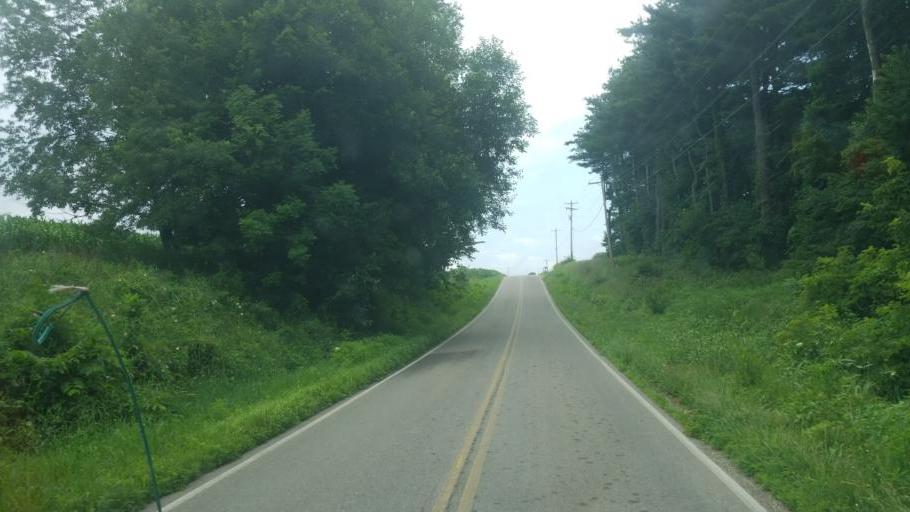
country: US
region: Ohio
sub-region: Wayne County
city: Wooster
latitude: 40.8651
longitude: -81.9999
